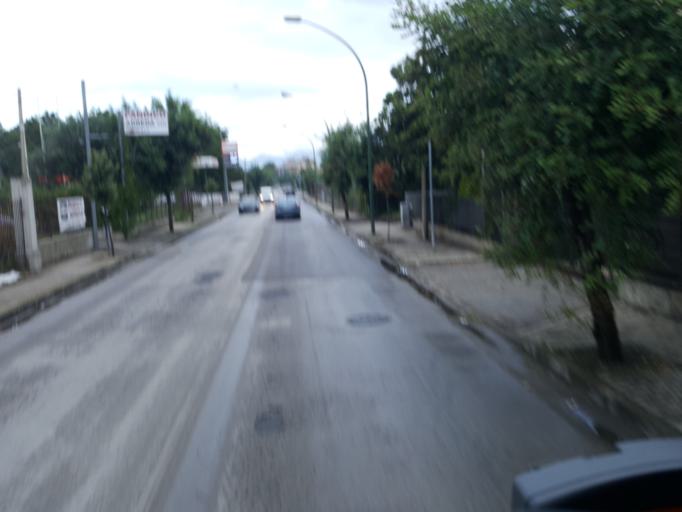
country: IT
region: Campania
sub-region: Provincia di Napoli
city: Palma Campania
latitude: 40.8630
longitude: 14.5486
